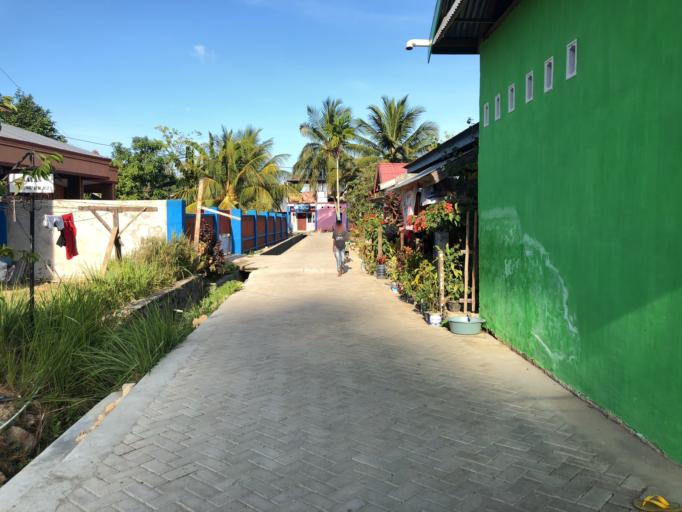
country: ID
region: Sulawesi Tenggara
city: Kendari
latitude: -3.9622
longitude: 122.6088
